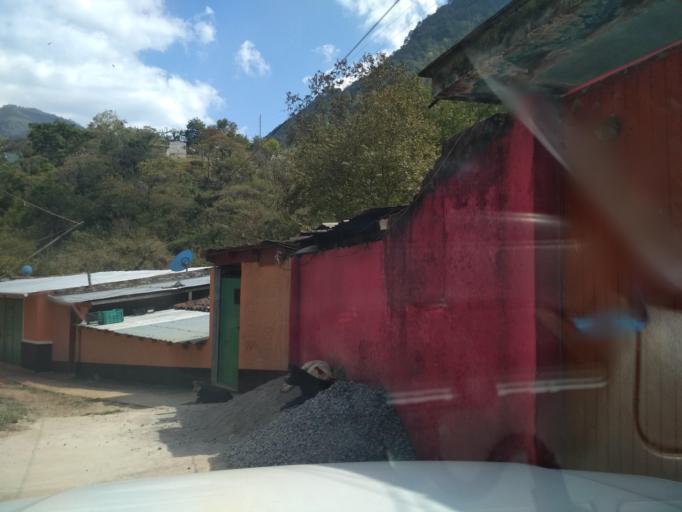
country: MX
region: Veracruz
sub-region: Tlilapan
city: Tonalixco
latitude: 18.7878
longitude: -97.0901
